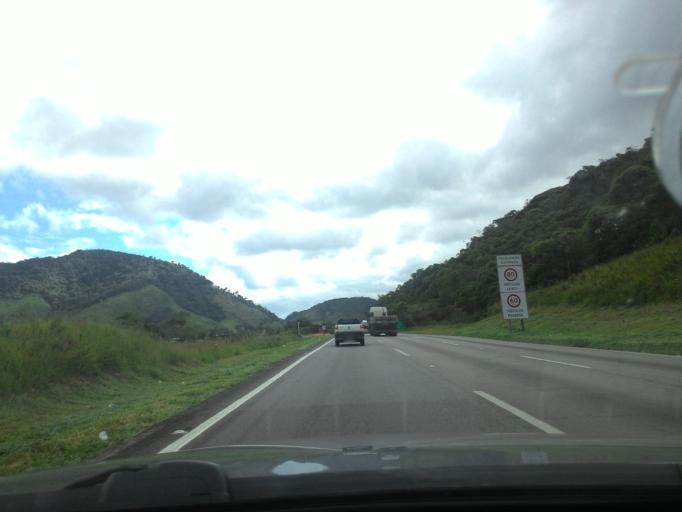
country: BR
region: Sao Paulo
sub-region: Cajati
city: Cajati
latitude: -24.8870
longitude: -48.2293
